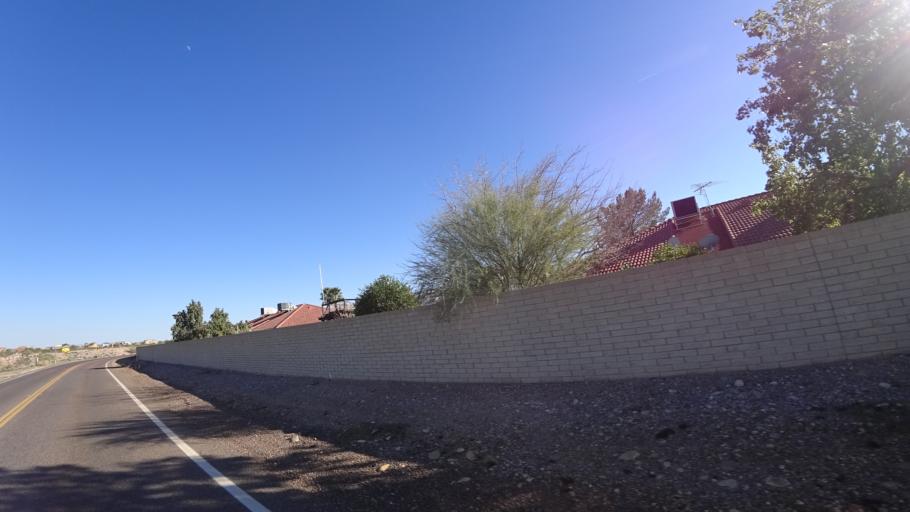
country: US
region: Arizona
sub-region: Maricopa County
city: Sun City West
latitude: 33.6819
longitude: -112.3279
